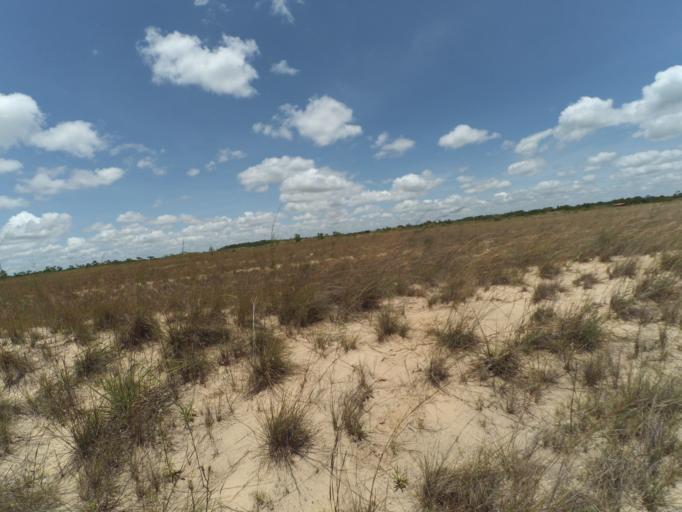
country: BO
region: Santa Cruz
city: Santa Cruz de la Sierra
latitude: -17.9385
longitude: -63.1597
